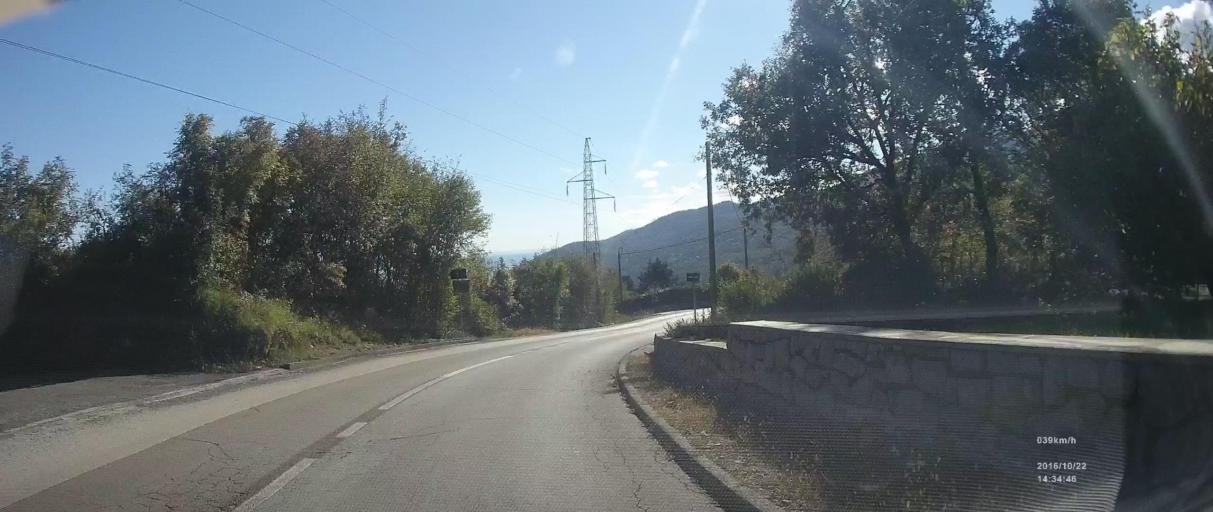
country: HR
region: Primorsko-Goranska
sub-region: Grad Opatija
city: Opatija
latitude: 45.3285
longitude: 14.2761
